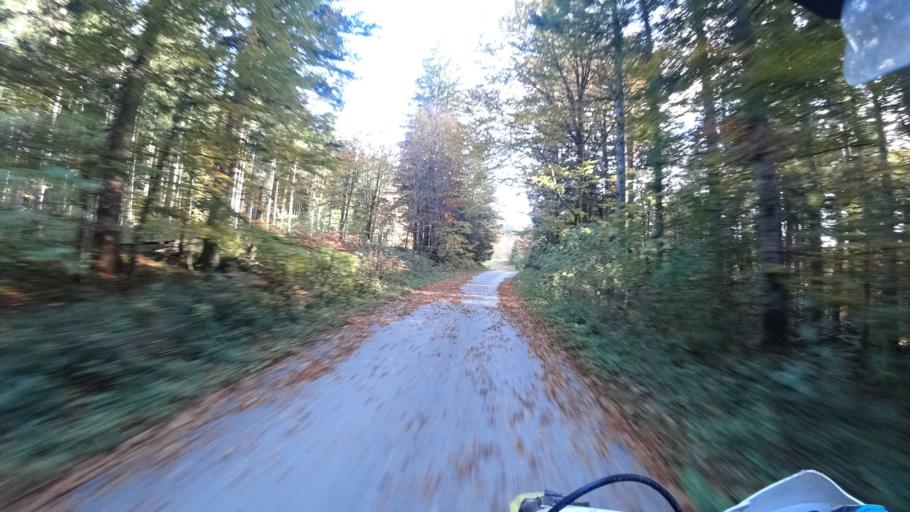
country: HR
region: Karlovacka
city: Plaski
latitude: 44.9789
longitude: 15.4011
